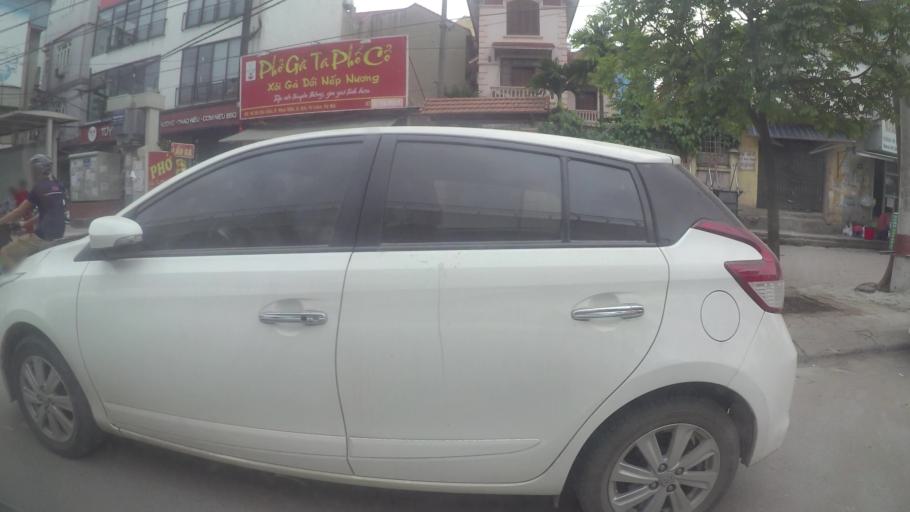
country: VN
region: Ha Noi
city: Cau Dien
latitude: 21.0452
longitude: 105.7514
